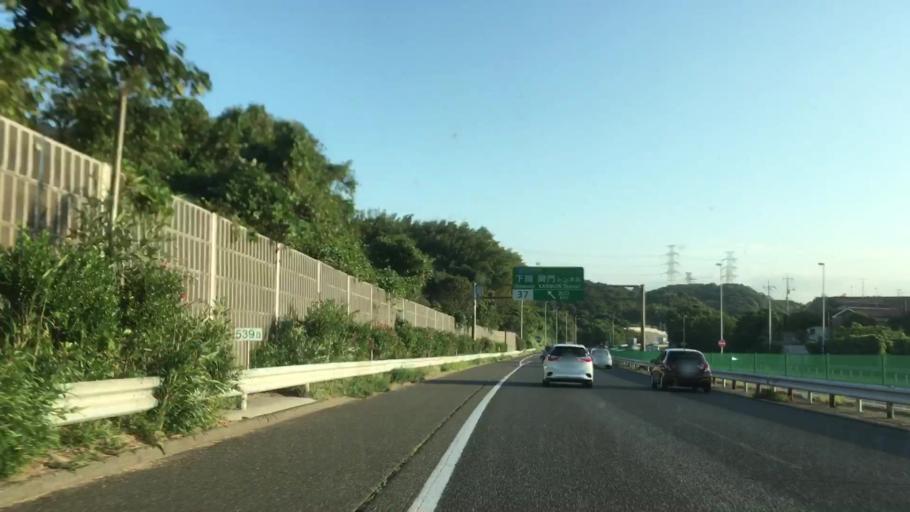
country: JP
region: Yamaguchi
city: Shimonoseki
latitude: 33.9815
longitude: 130.9524
